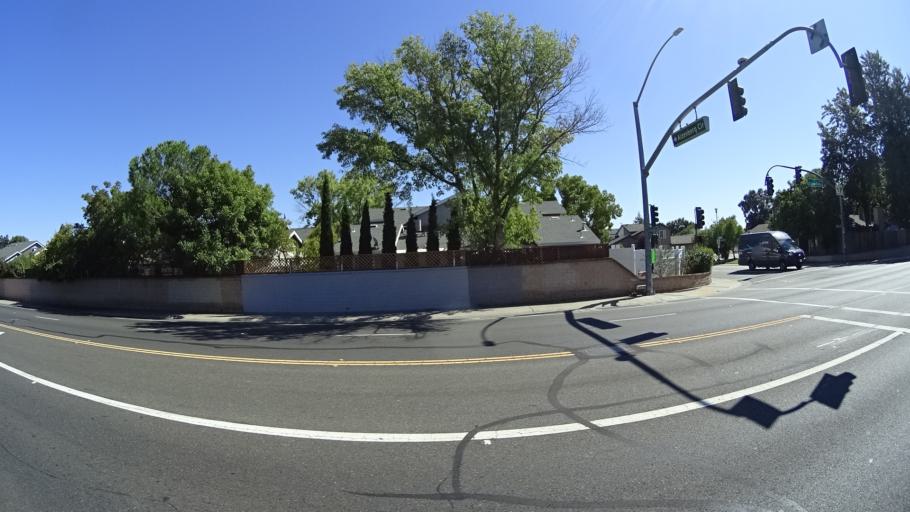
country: US
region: California
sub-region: Sacramento County
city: Elk Grove
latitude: 38.4194
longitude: -121.3717
